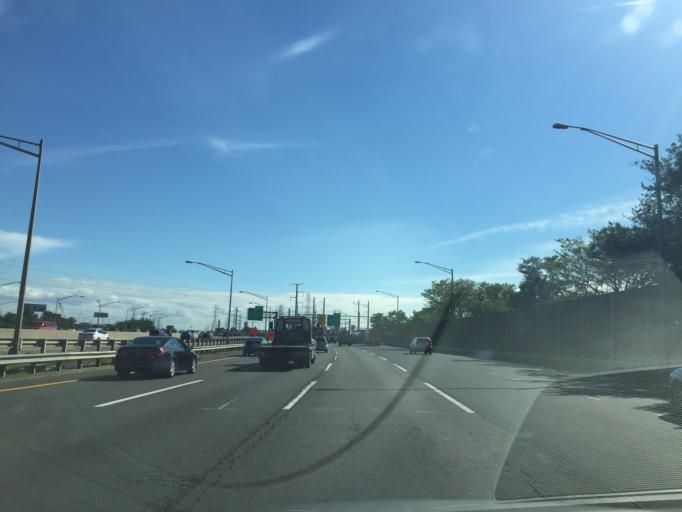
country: US
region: New Jersey
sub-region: Union County
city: Elizabeth
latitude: 40.6490
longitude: -74.2013
